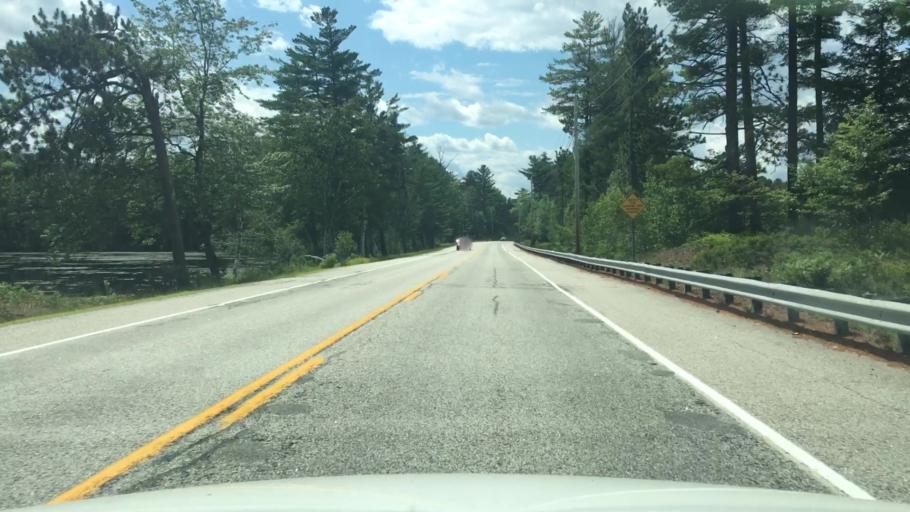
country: US
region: Maine
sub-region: Oxford County
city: Bethel
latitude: 44.3988
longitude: -70.6889
